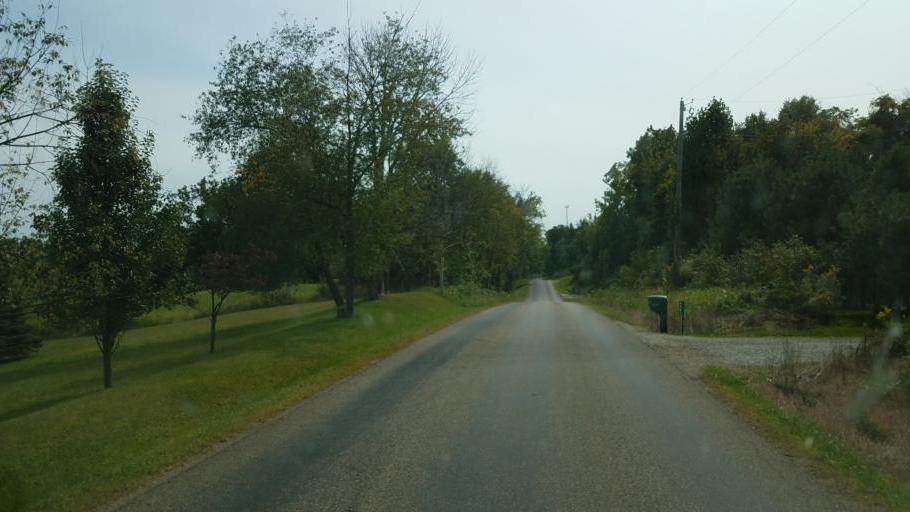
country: US
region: Ohio
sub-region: Knox County
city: Centerburg
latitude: 40.3710
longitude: -82.6053
